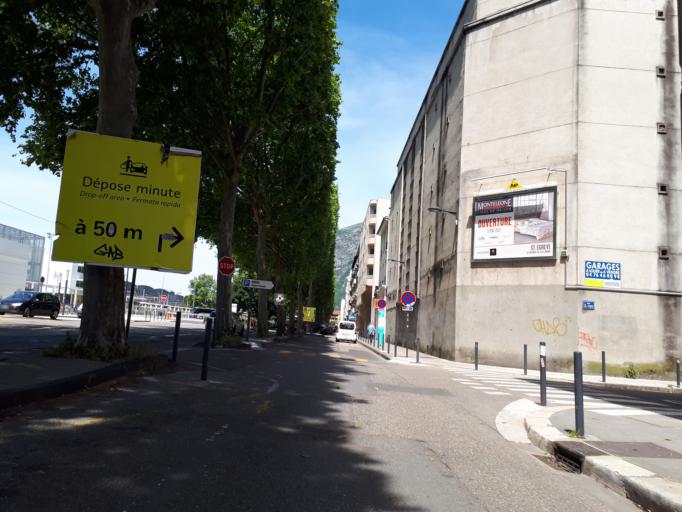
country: FR
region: Rhone-Alpes
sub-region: Departement de l'Isere
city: Saint-Martin-le-Vinoux
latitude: 45.1919
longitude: 5.7152
